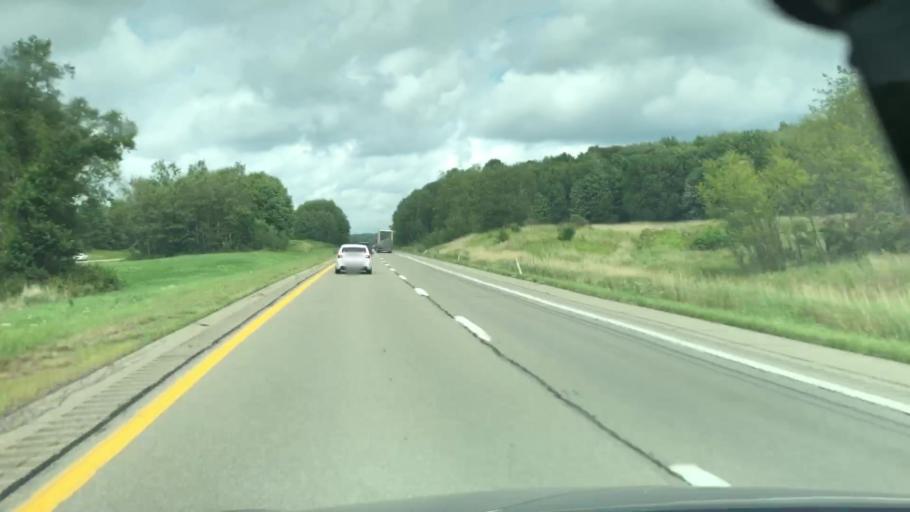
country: US
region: Pennsylvania
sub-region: Erie County
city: Edinboro
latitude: 41.7682
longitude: -80.1925
